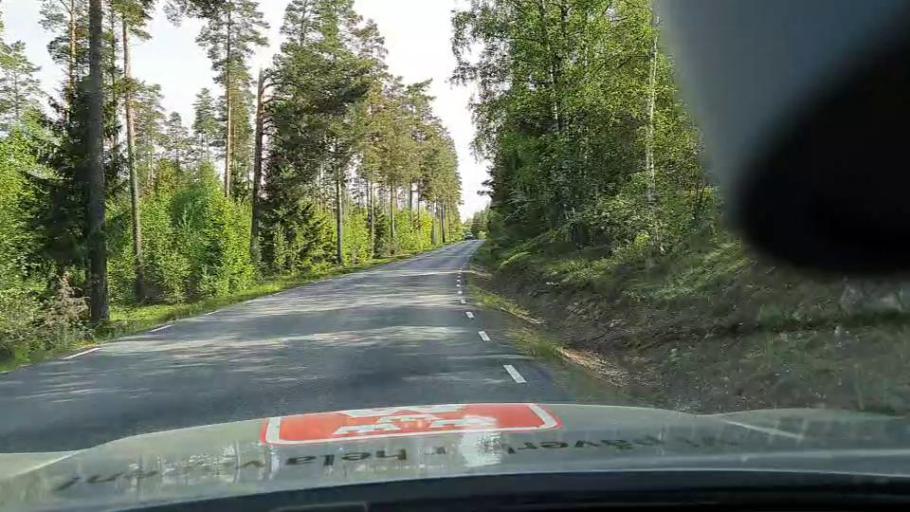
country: SE
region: Soedermanland
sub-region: Eskilstuna Kommun
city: Arla
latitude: 59.2570
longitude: 16.7111
